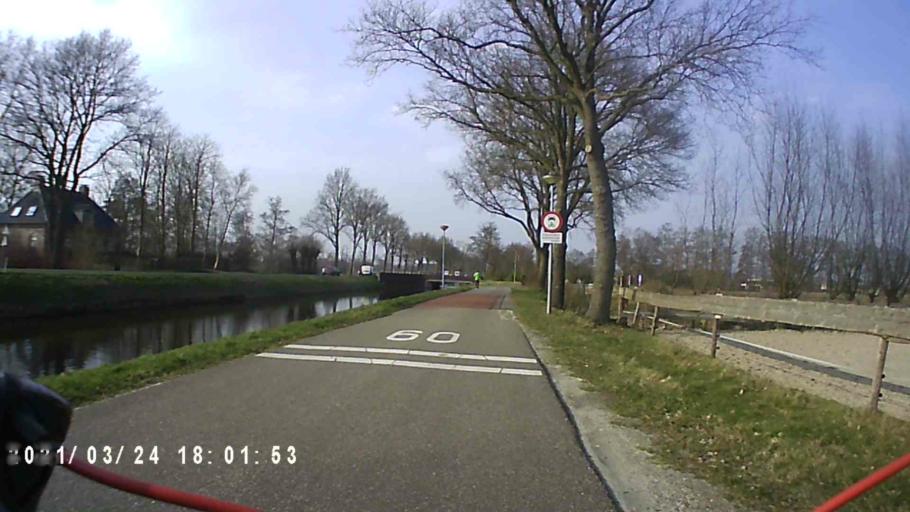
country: NL
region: Groningen
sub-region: Gemeente Leek
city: Leek
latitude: 53.1380
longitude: 6.3609
